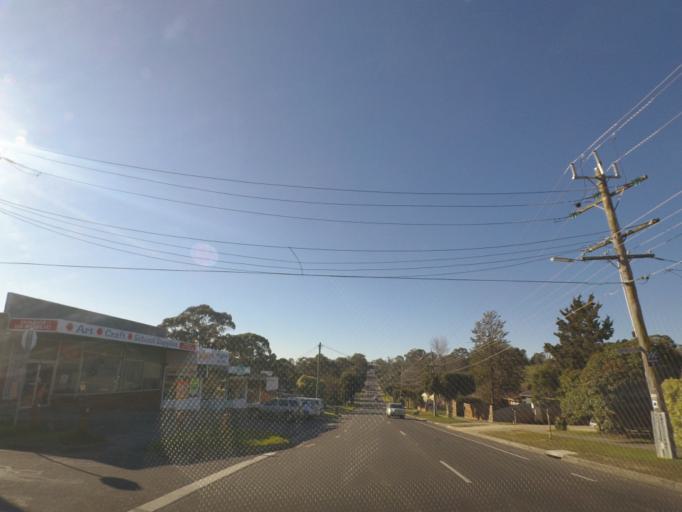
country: AU
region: Victoria
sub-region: Yarra Ranges
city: Kilsyth
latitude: -37.7965
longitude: 145.3134
